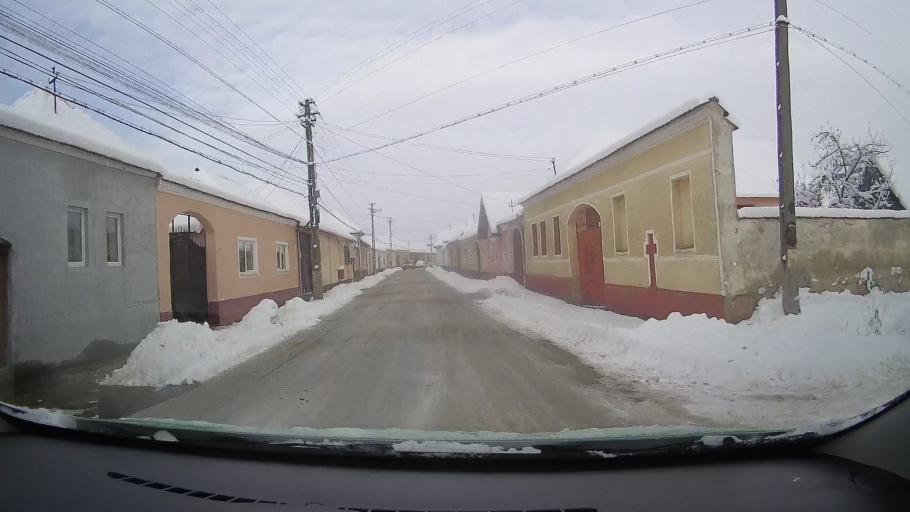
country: RO
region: Alba
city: Pianu de Sus
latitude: 45.8996
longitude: 23.4806
